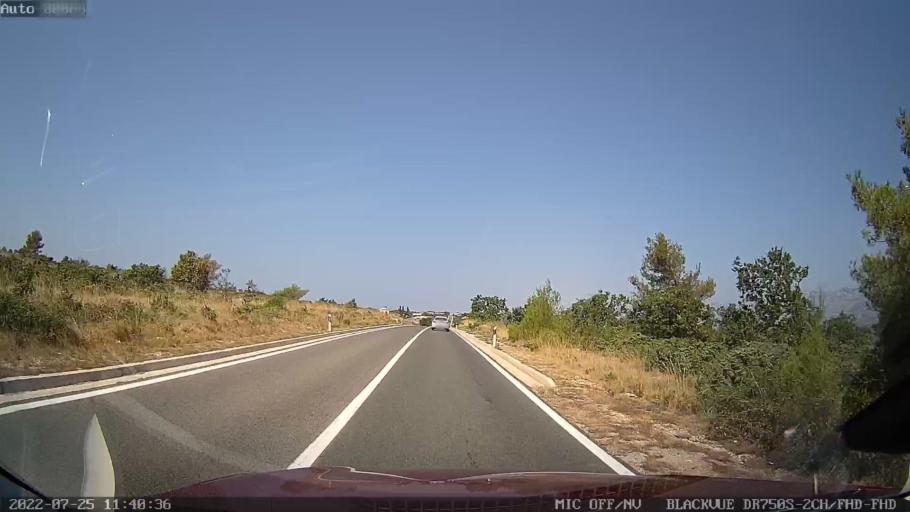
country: HR
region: Zadarska
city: Razanac
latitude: 44.2642
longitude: 15.3576
